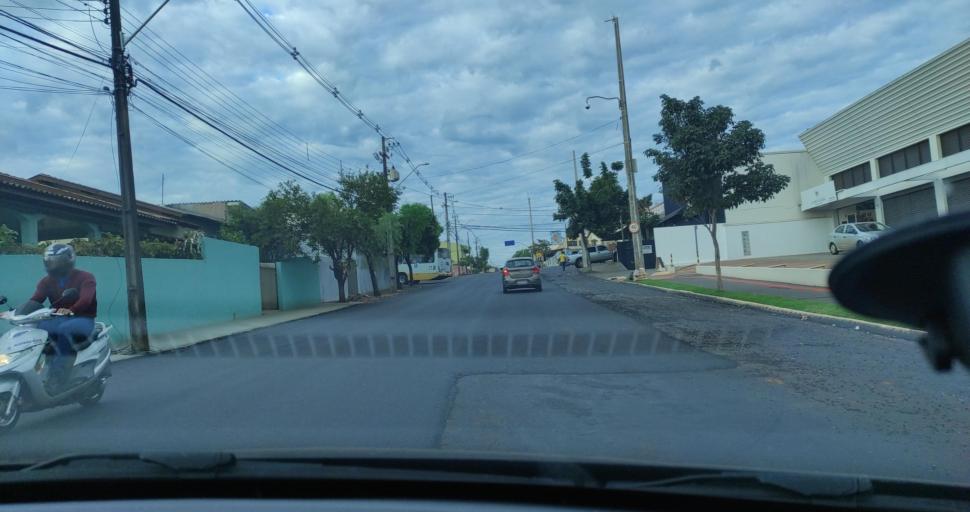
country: BR
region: Parana
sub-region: Ibipora
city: Ibipora
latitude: -23.2541
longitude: -51.0503
